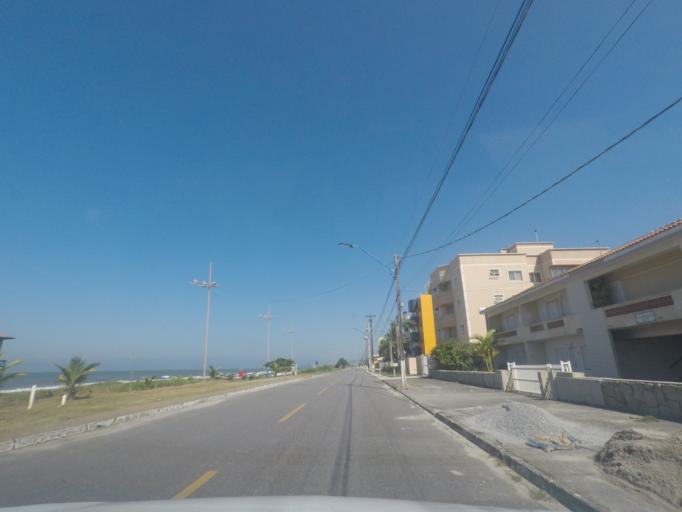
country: BR
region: Parana
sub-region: Pontal Do Parana
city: Pontal do Parana
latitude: -25.7607
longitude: -48.5065
